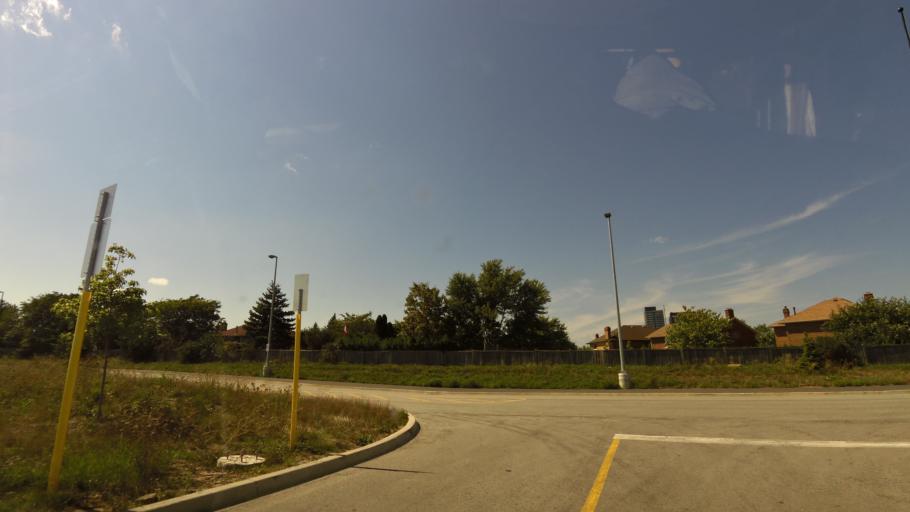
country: CA
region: Ontario
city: Mississauga
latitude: 43.5530
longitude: -79.7008
